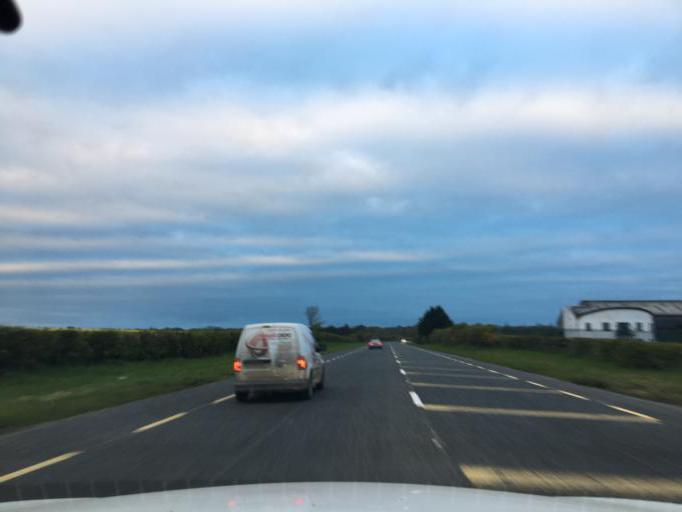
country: IE
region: Leinster
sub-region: Loch Garman
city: Loch Garman
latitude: 52.3033
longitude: -6.4637
